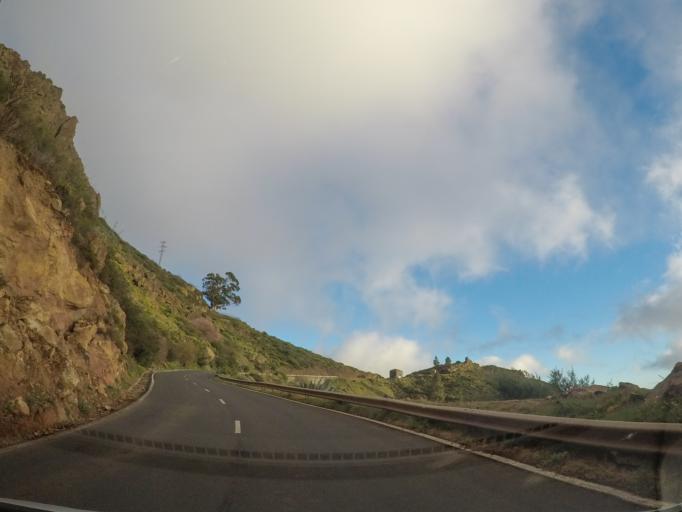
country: ES
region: Canary Islands
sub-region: Provincia de Santa Cruz de Tenerife
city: Alajero
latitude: 28.0880
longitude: -17.2511
